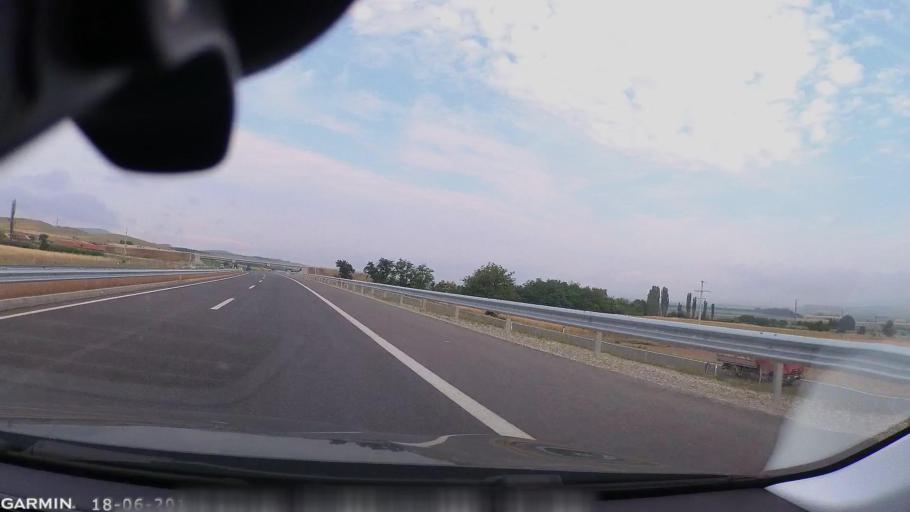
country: MK
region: Stip
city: Shtip
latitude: 41.7897
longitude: 22.1096
